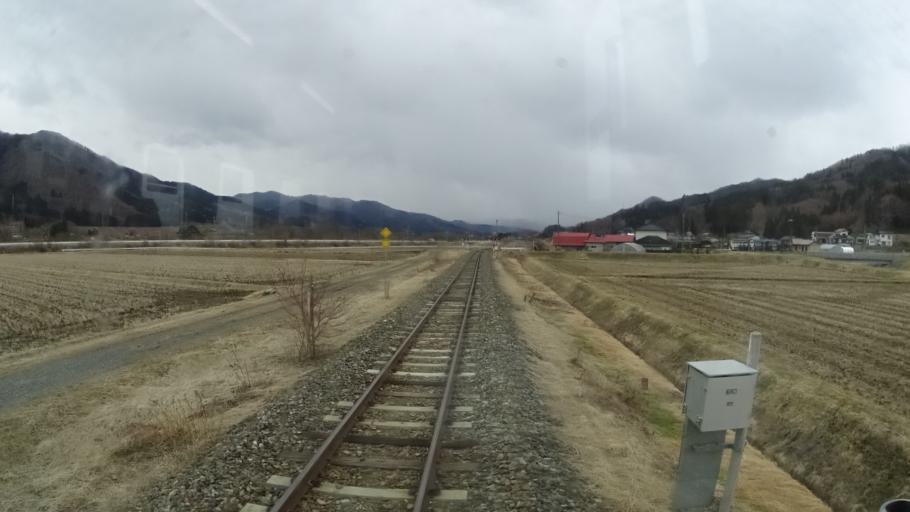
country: JP
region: Iwate
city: Tono
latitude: 39.3210
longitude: 141.4495
